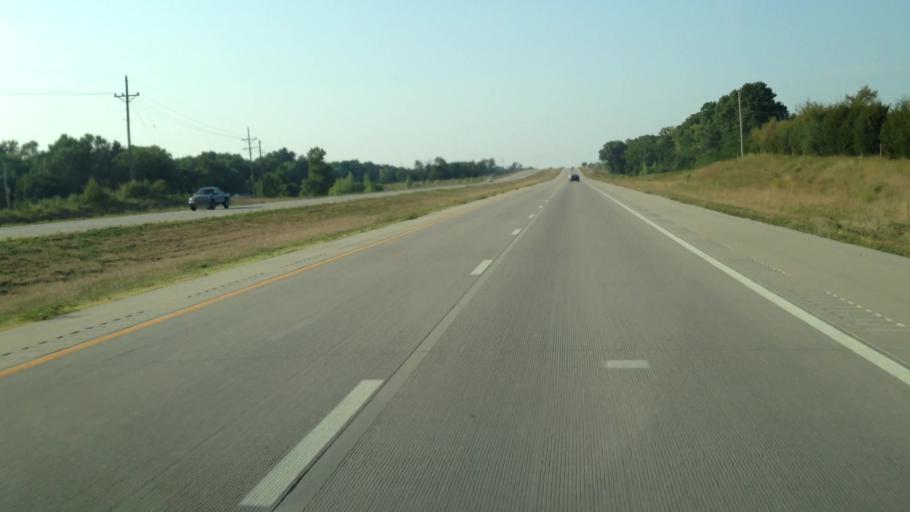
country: US
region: Kansas
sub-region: Douglas County
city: Baldwin City
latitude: 38.7519
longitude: -95.2677
